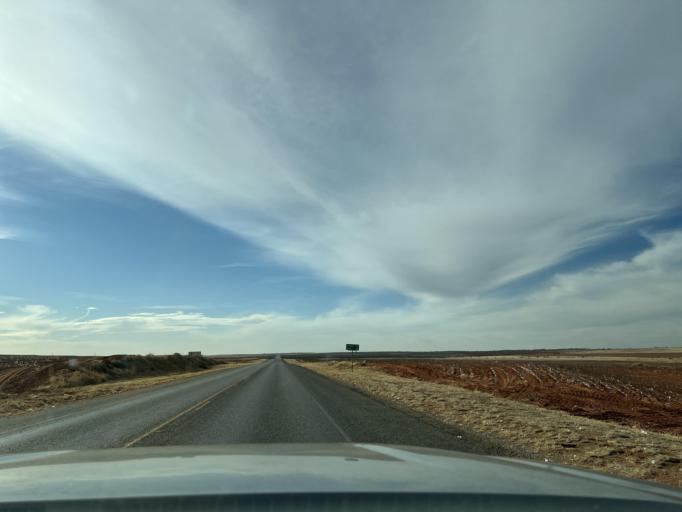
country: US
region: Texas
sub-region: Fisher County
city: Rotan
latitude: 32.7405
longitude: -100.4924
